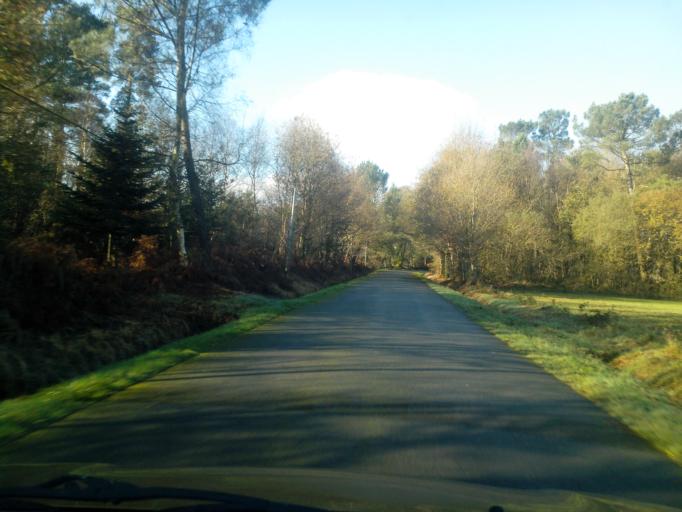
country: FR
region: Brittany
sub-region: Departement du Morbihan
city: Molac
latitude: 47.7270
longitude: -2.4014
